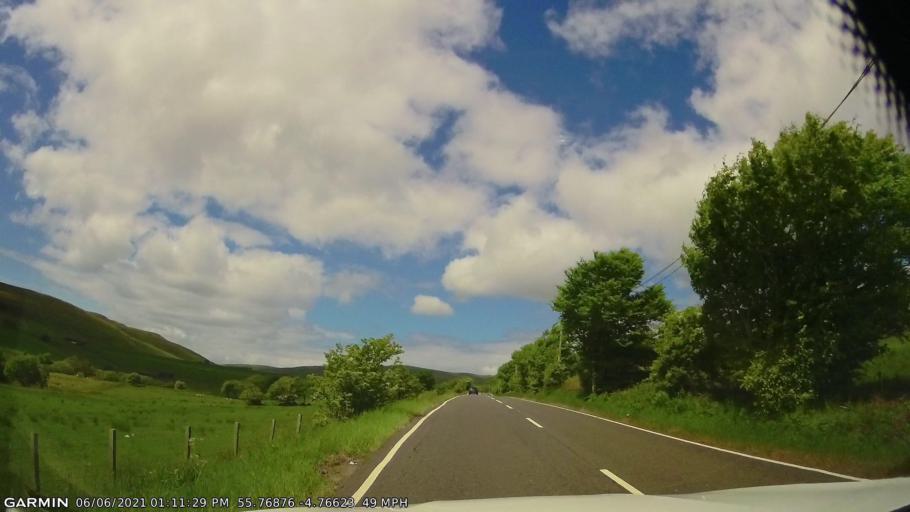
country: GB
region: Scotland
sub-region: North Ayrshire
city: Dalry
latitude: 55.7688
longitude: -4.7662
